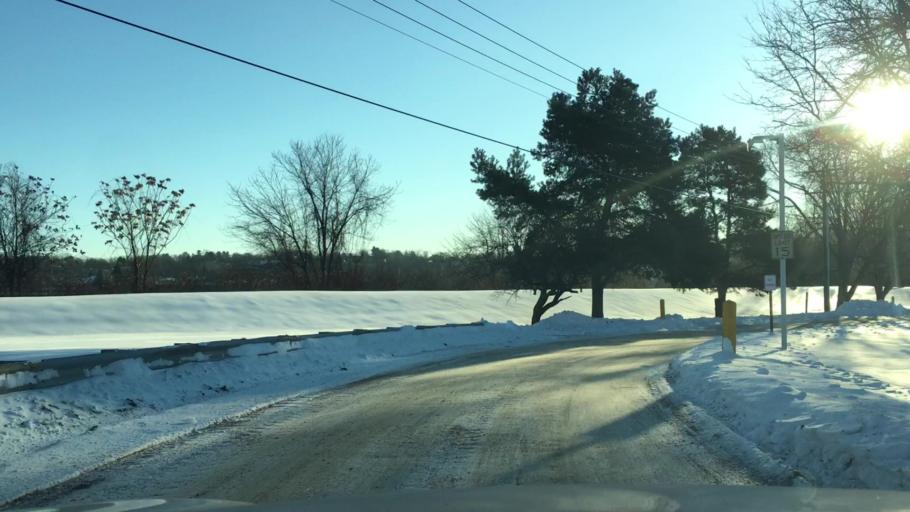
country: US
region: Massachusetts
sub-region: Hampden County
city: Springfield
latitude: 42.0901
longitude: -72.5890
